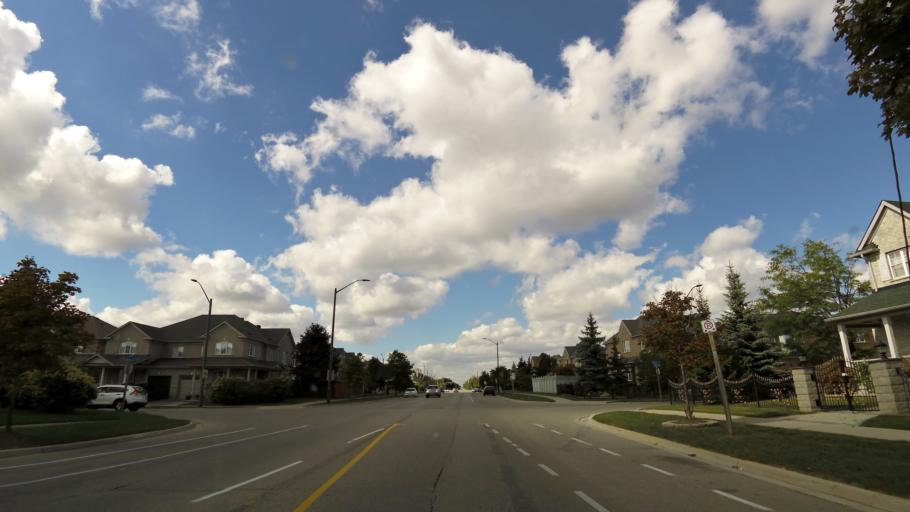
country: CA
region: Ontario
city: Mississauga
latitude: 43.5621
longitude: -79.7461
